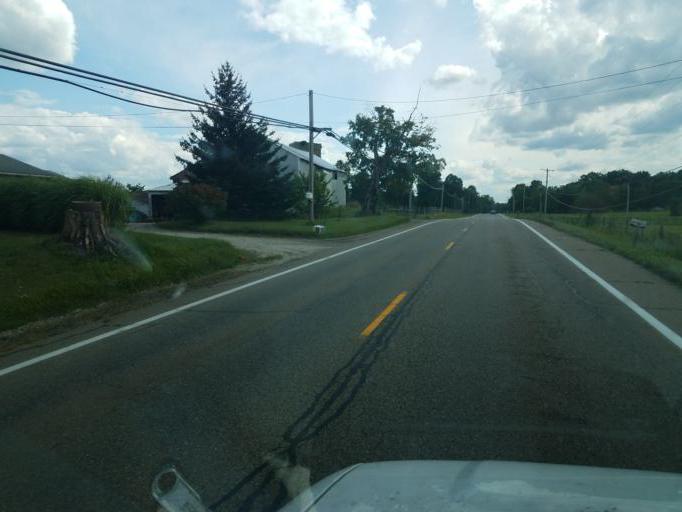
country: US
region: Ohio
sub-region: Portage County
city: Ravenna
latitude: 41.0721
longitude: -81.2435
